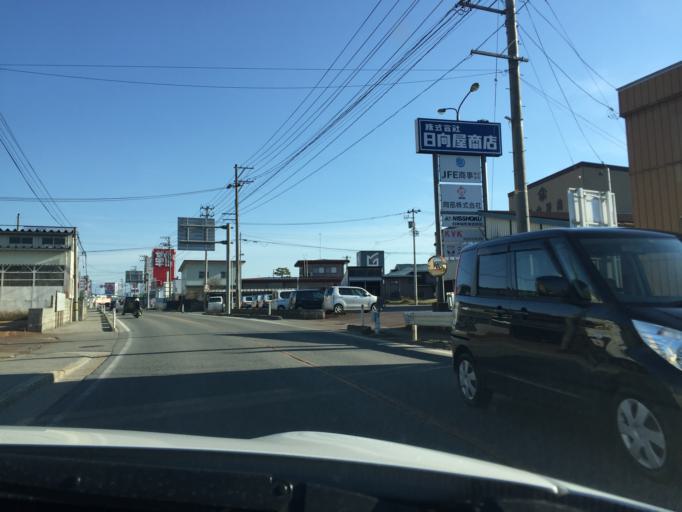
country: JP
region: Yamagata
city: Nagai
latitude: 38.0943
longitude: 140.0415
